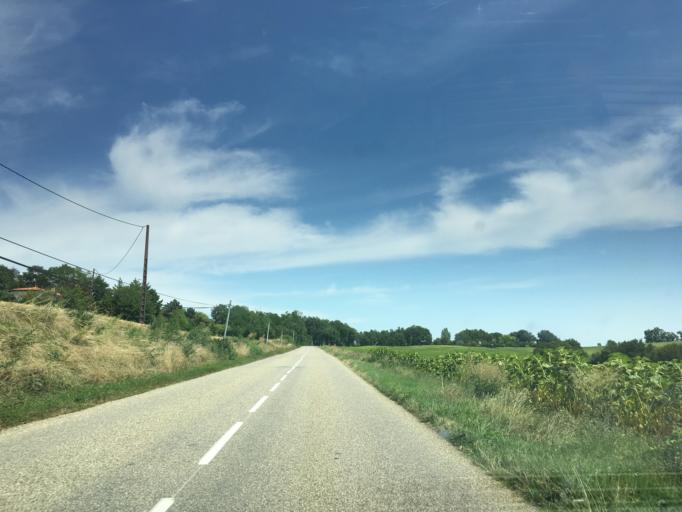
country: FR
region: Midi-Pyrenees
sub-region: Departement du Gers
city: Fleurance
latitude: 43.8655
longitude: 0.7056
